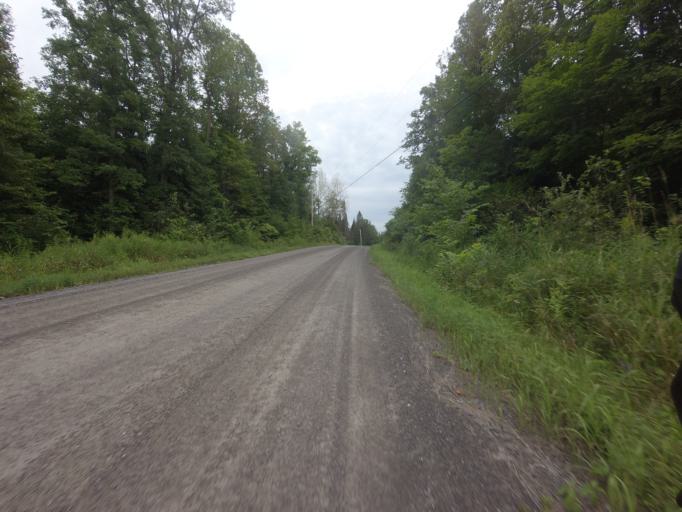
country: CA
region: Ontario
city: Carleton Place
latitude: 45.1635
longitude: -76.2719
